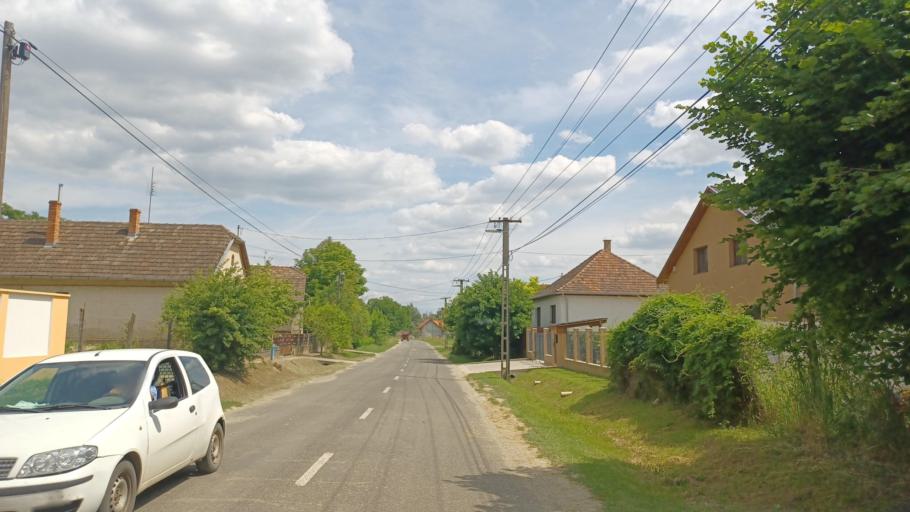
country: HU
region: Tolna
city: Simontornya
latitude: 46.6763
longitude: 18.5452
